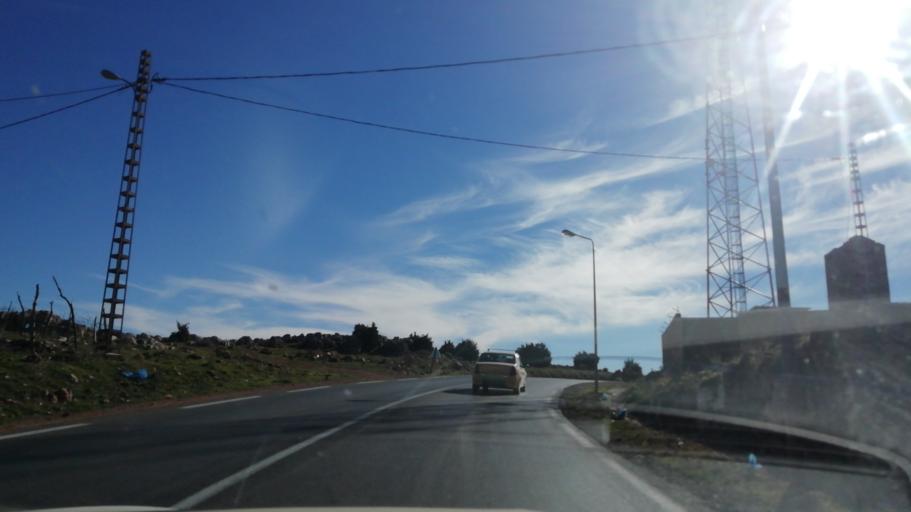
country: DZ
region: Tlemcen
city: Mansoura
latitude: 34.7536
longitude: -1.3440
